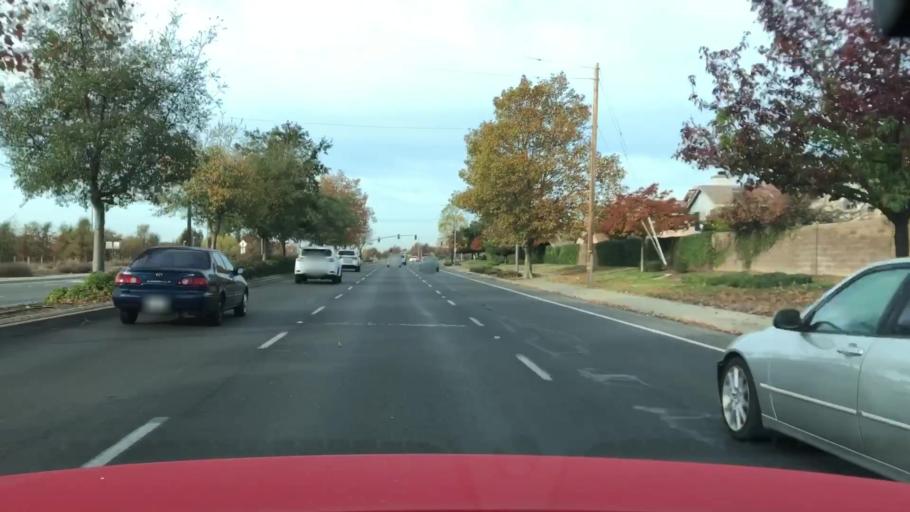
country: US
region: California
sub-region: Sacramento County
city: Laguna
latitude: 38.4527
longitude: -121.3931
